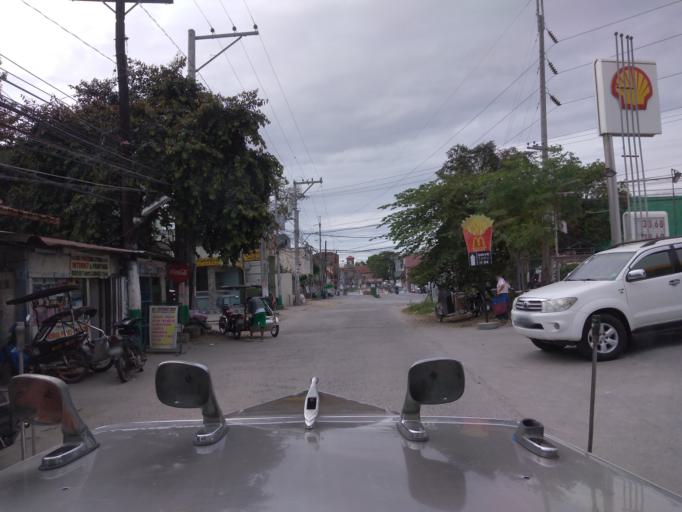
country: PH
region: Central Luzon
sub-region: Province of Pampanga
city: Mexico
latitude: 15.0642
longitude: 120.7222
